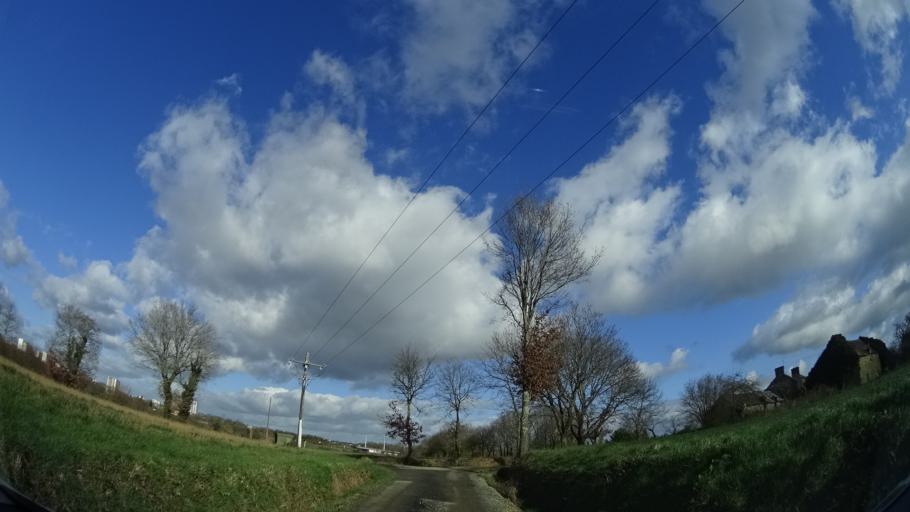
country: FR
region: Brittany
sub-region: Departement d'Ille-et-Vilaine
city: Chantepie
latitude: 48.0785
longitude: -1.6423
